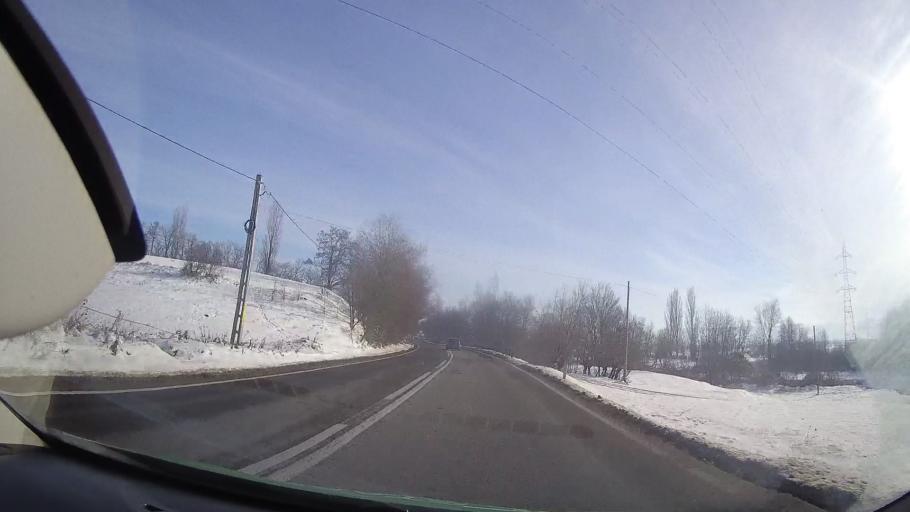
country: RO
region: Neamt
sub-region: Comuna Ghindaoani
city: Ghindaoani
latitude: 47.0736
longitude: 26.3584
